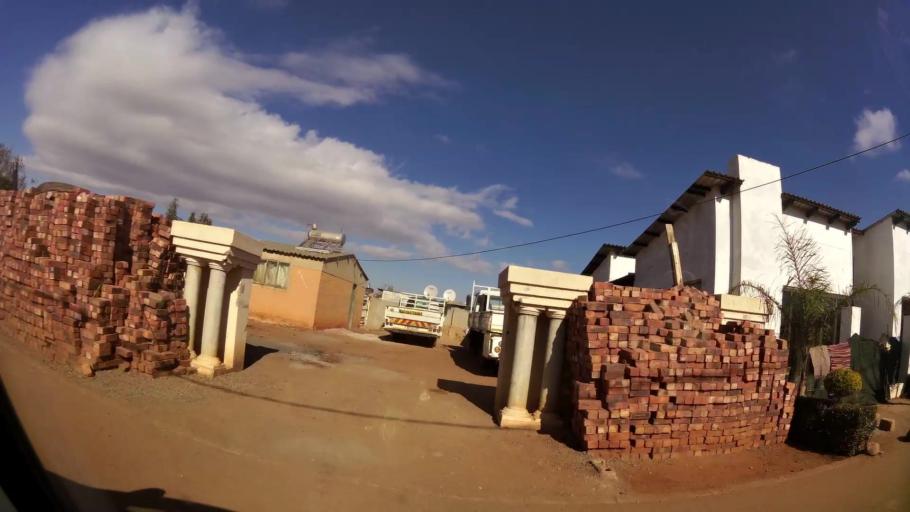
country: ZA
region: Gauteng
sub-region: City of Tshwane Metropolitan Municipality
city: Cullinan
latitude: -25.6965
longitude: 28.4170
